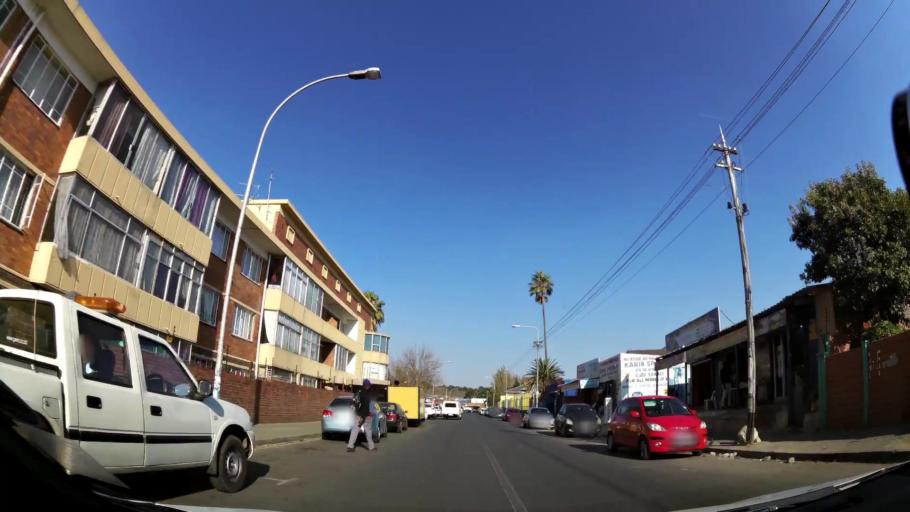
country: ZA
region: Gauteng
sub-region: City of Johannesburg Metropolitan Municipality
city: Johannesburg
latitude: -26.2374
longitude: 28.0263
